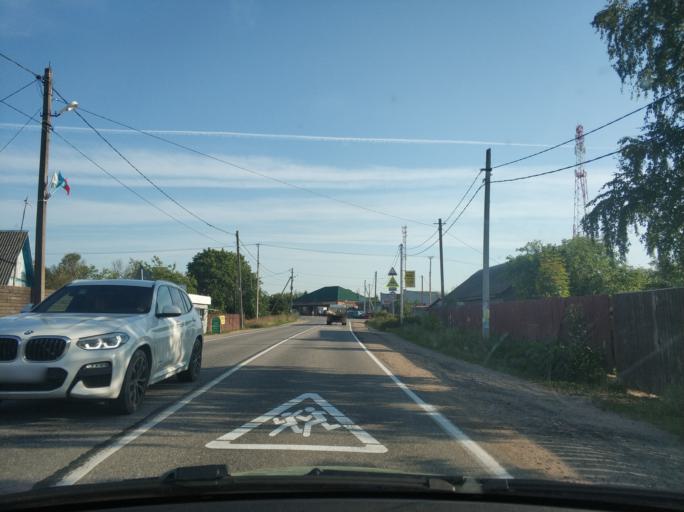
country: RU
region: Leningrad
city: Borisova Griva
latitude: 60.0895
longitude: 31.0189
